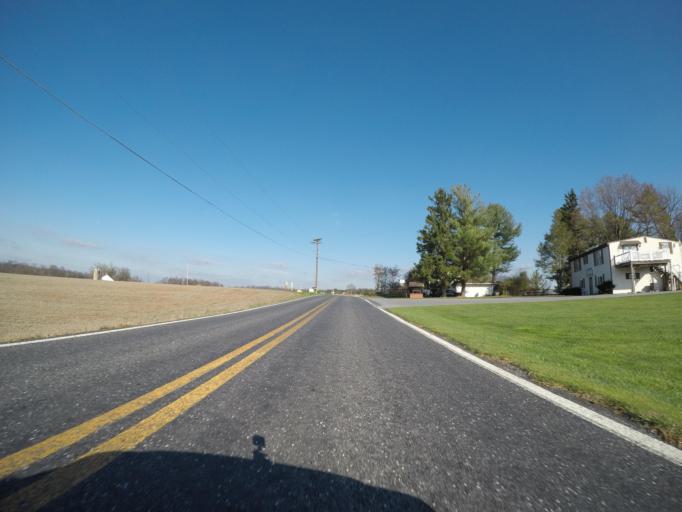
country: US
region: Maryland
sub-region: Carroll County
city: Hampstead
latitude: 39.5501
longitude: -76.8799
